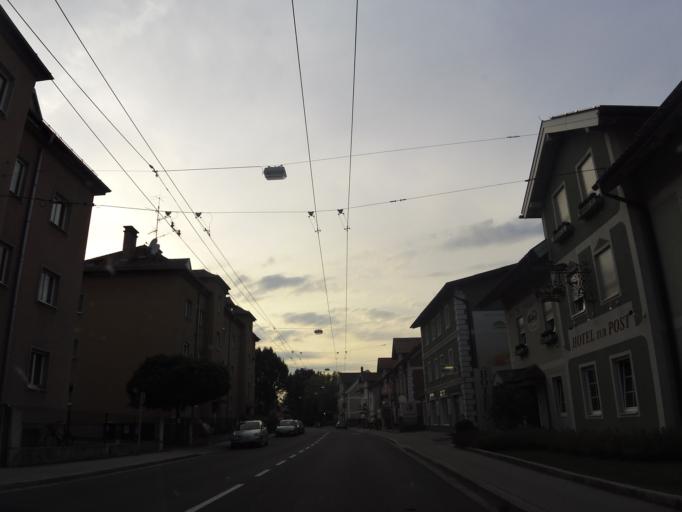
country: AT
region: Salzburg
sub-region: Salzburg Stadt
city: Salzburg
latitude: 47.7983
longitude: 13.0199
